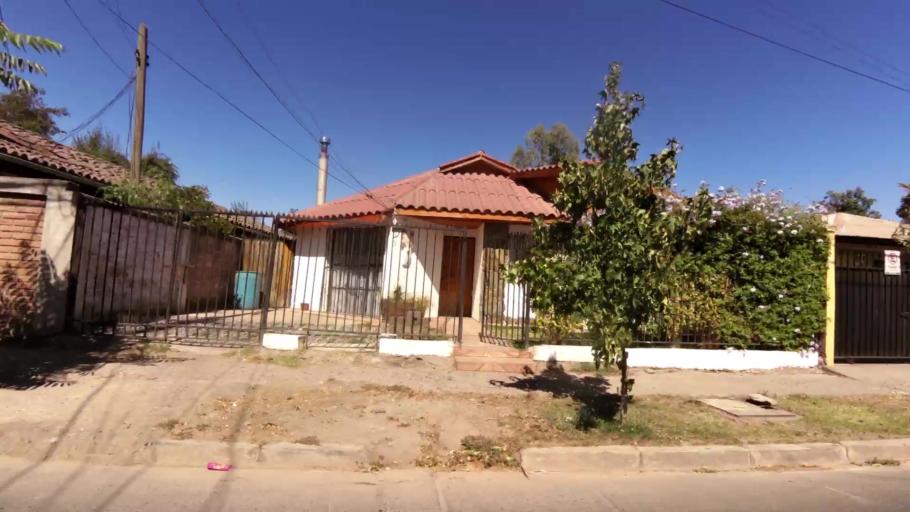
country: CL
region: O'Higgins
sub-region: Provincia de Colchagua
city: Chimbarongo
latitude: -34.5918
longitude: -70.9959
